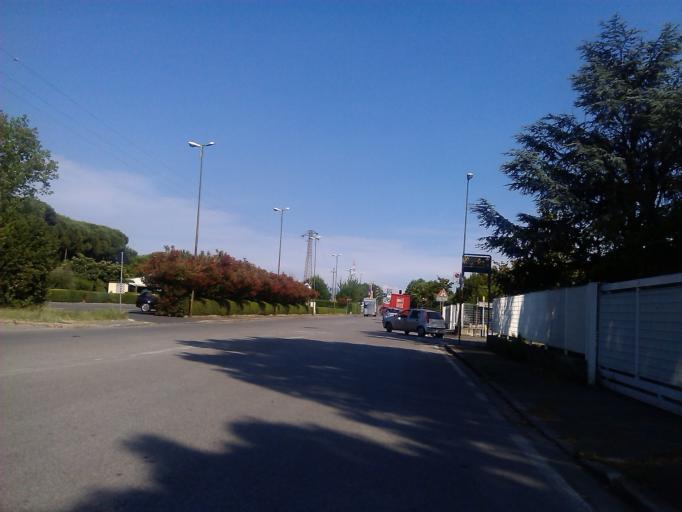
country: IT
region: Tuscany
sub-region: Province of Florence
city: Campi Bisenzio
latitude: 43.8500
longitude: 11.1300
